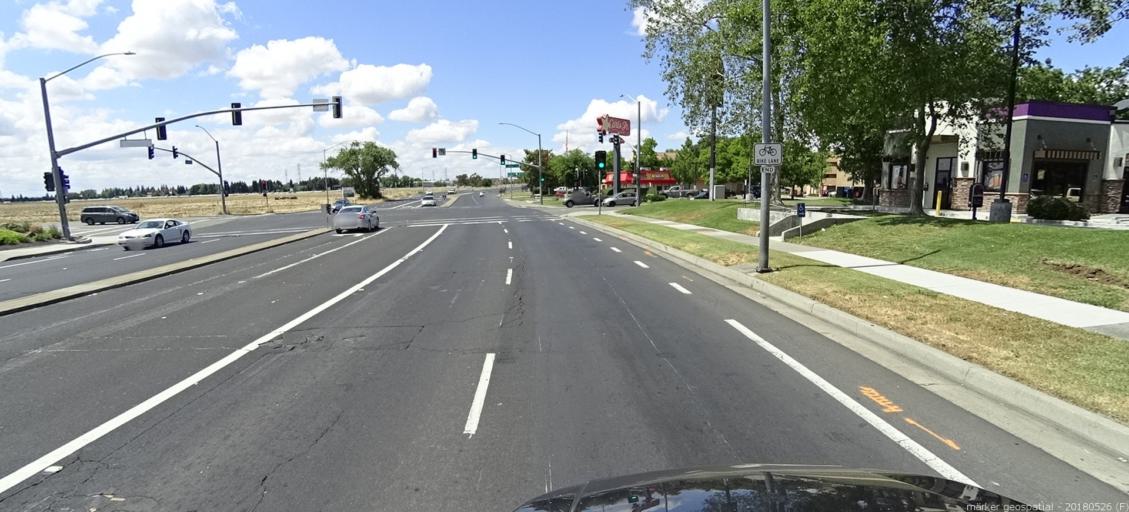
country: US
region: California
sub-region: Sacramento County
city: Sacramento
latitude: 38.6362
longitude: -121.4759
